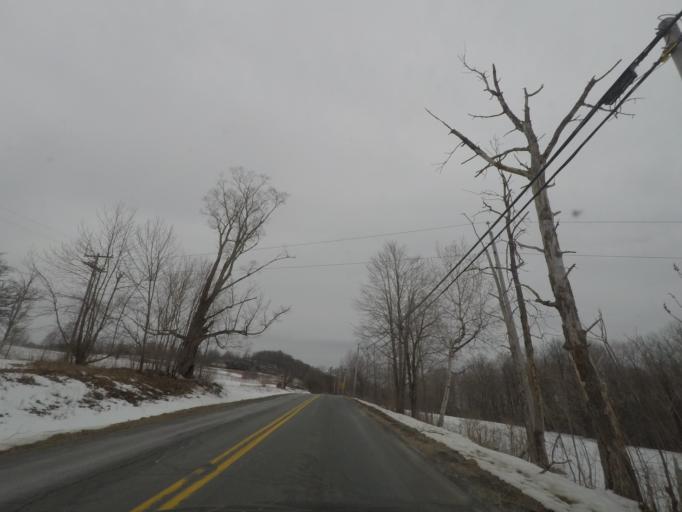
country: US
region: Massachusetts
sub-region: Berkshire County
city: Lanesborough
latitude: 42.5661
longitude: -73.3800
